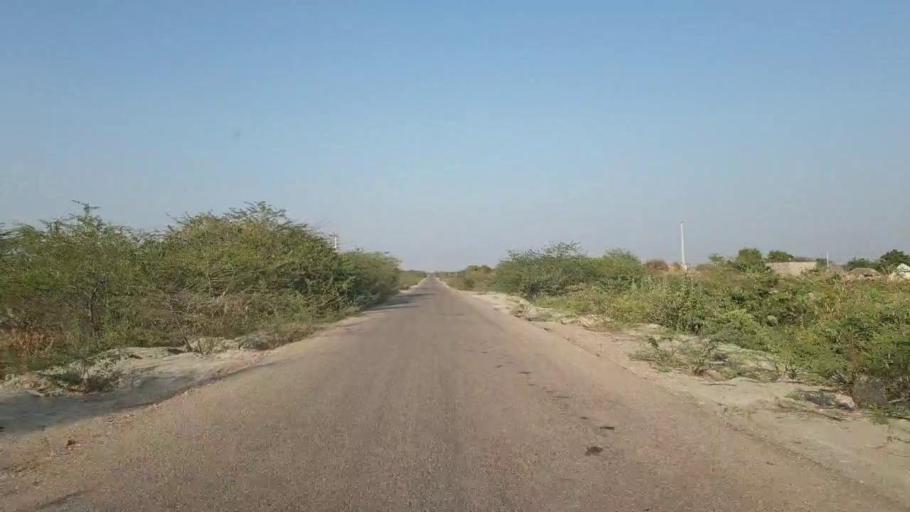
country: PK
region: Sindh
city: Chor
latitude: 25.5641
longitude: 69.7995
